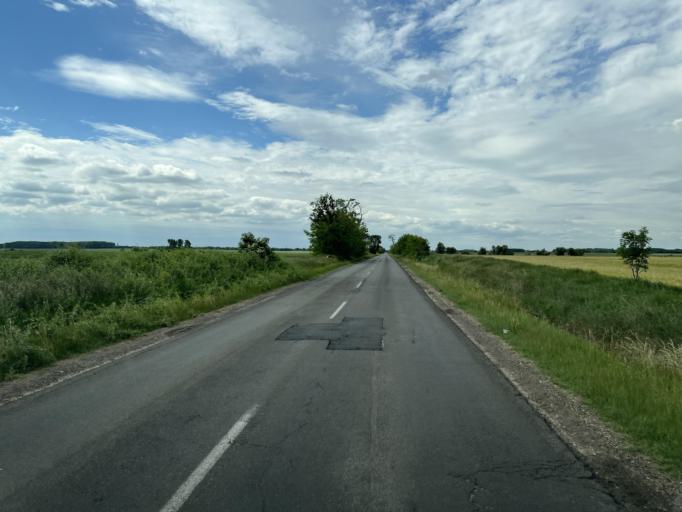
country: HU
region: Pest
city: Szentlorinckata
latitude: 47.5090
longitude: 19.7433
